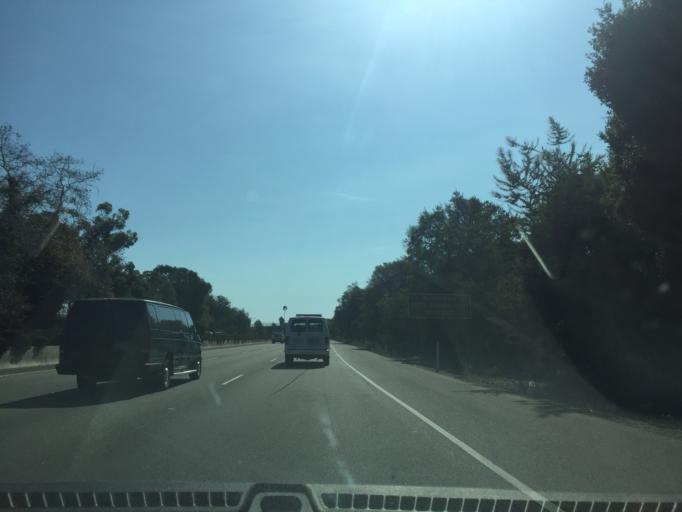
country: US
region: California
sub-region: Santa Barbara County
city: Santa Barbara
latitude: 34.4233
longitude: -119.7174
